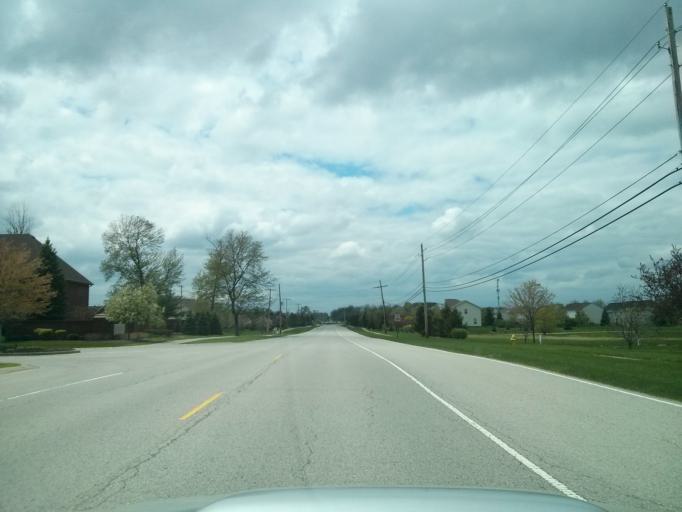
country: US
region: Indiana
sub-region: Hamilton County
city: Fishers
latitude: 39.9712
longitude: -86.0631
